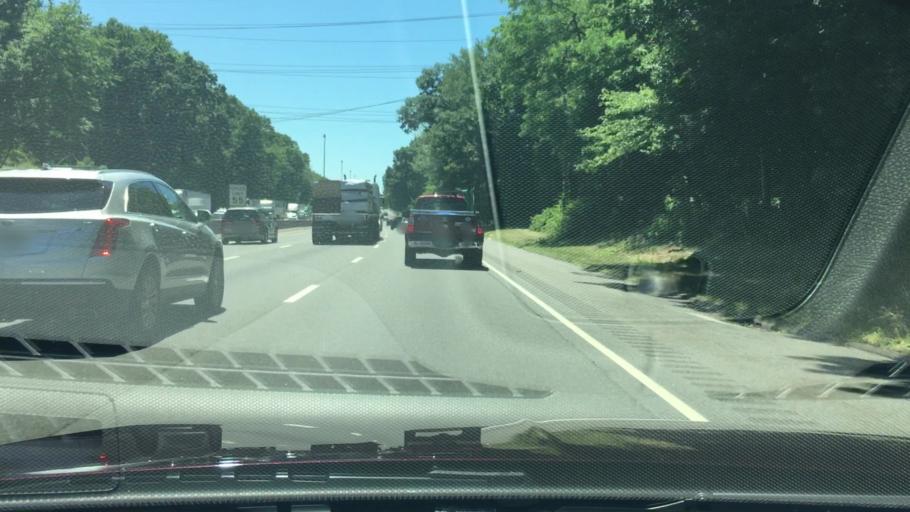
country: US
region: Connecticut
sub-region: Fairfield County
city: Darien
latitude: 41.0982
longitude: -73.4416
